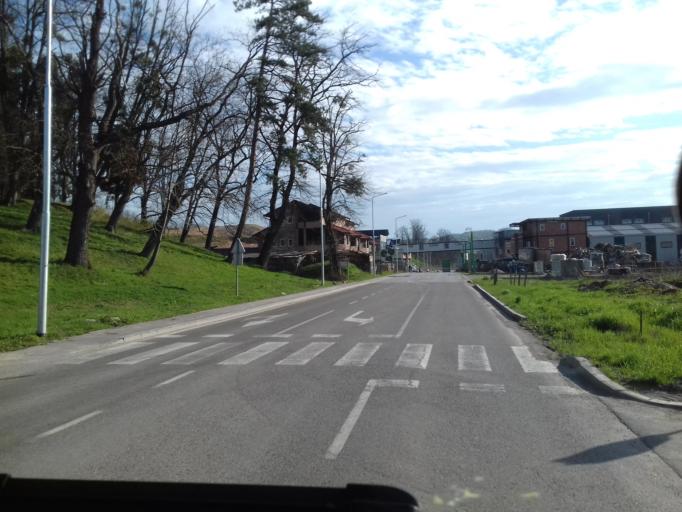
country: BA
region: Federation of Bosnia and Herzegovina
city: Tesanj
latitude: 44.6336
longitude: 18.0073
